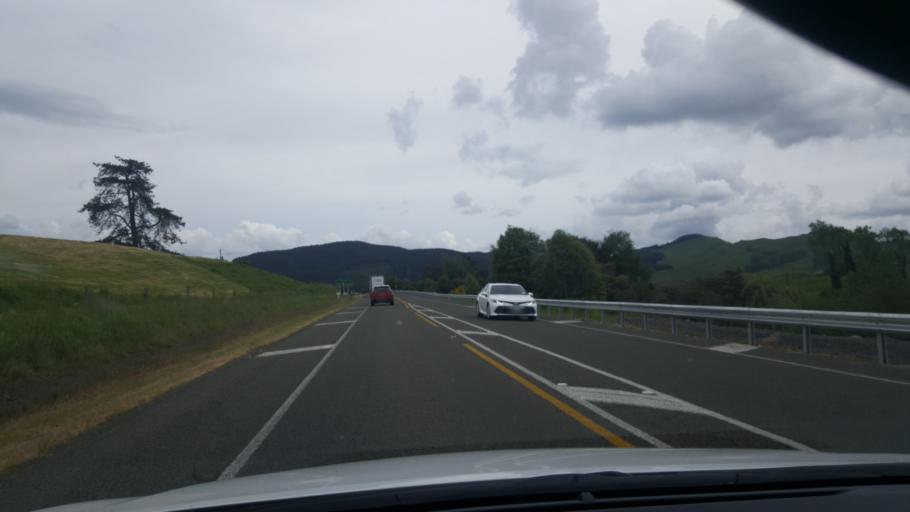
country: NZ
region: Bay of Plenty
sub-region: Rotorua District
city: Rotorua
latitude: -38.3349
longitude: 176.3665
